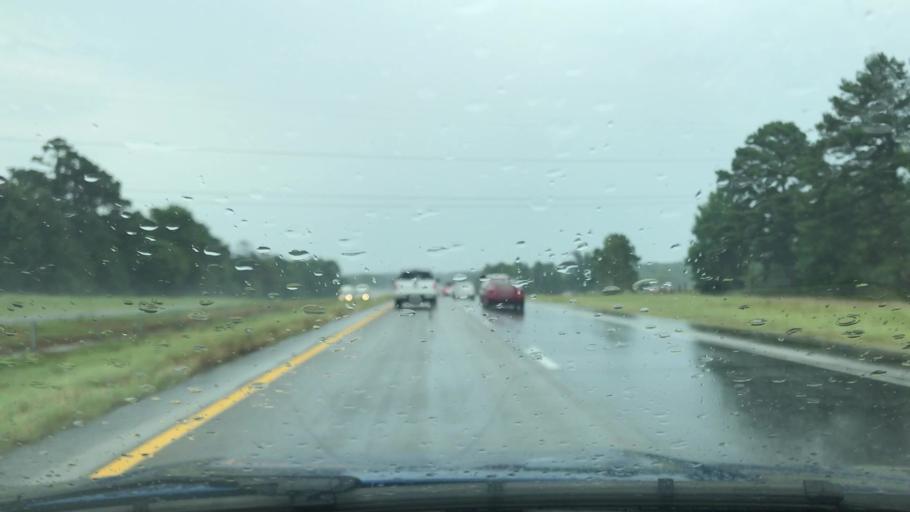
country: US
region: Texas
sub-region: Harrison County
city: Waskom
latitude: 32.4900
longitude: -94.1453
